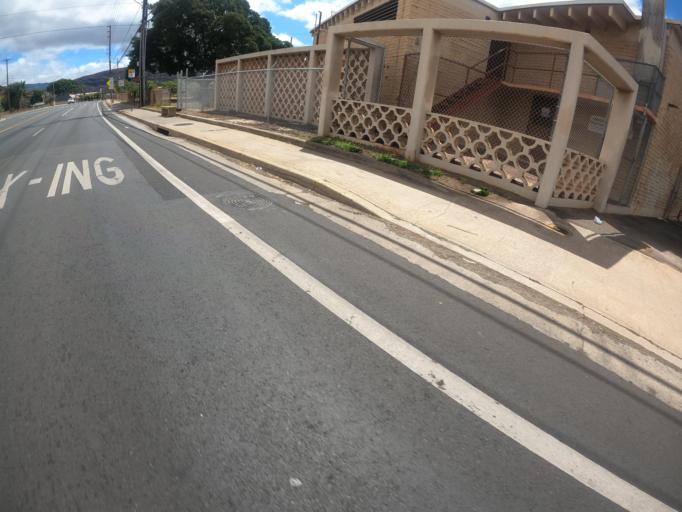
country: US
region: Hawaii
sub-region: Honolulu County
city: Waianae
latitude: 21.4496
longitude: -158.1910
